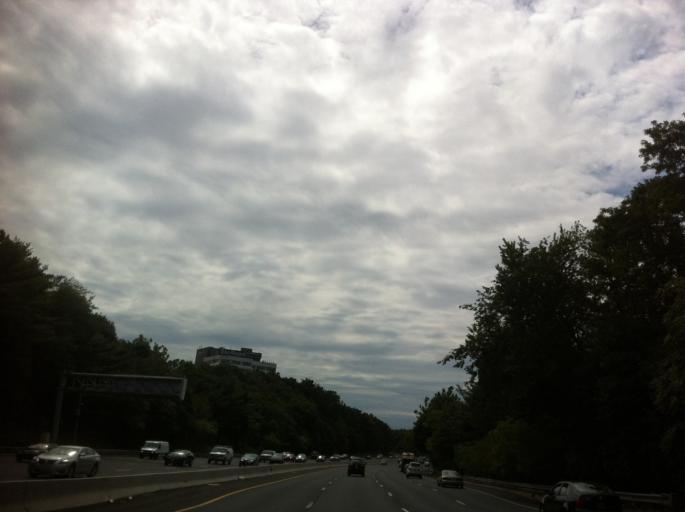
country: US
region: New Jersey
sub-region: Passaic County
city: Paterson
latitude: 40.9022
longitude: -74.1557
